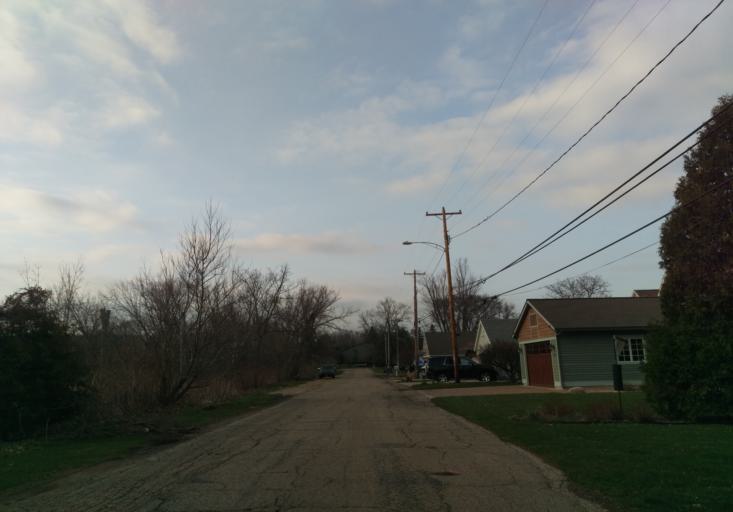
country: US
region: Wisconsin
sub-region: Dane County
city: Middleton
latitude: 43.1022
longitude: -89.4844
